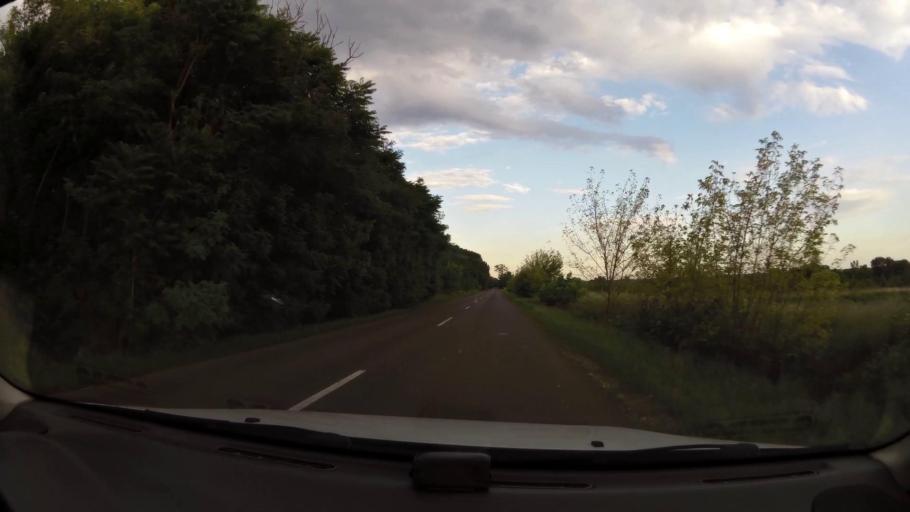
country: HU
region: Pest
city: Tapiobicske
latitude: 47.3802
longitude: 19.6622
